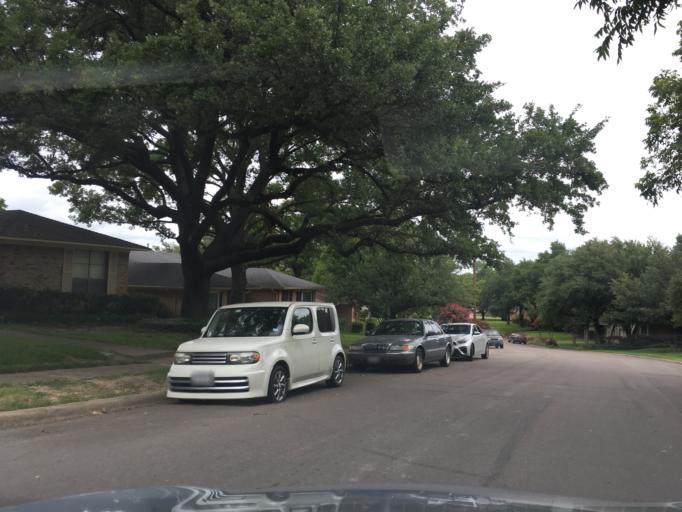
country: US
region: Texas
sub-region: Dallas County
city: Highland Park
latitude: 32.8621
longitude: -96.7425
